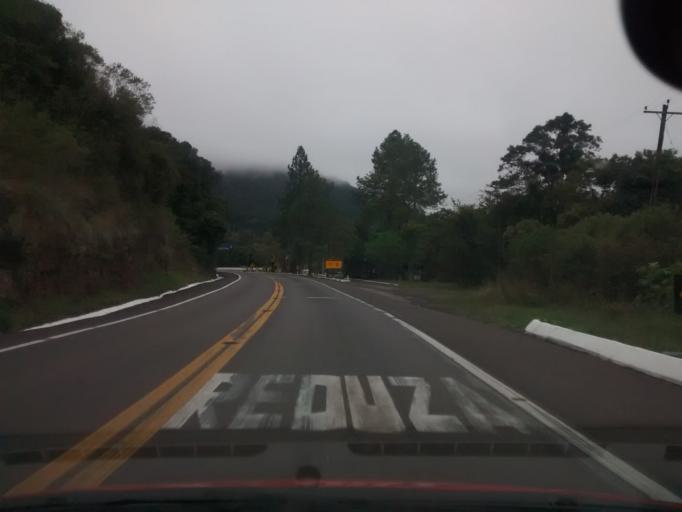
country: BR
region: Rio Grande do Sul
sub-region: Vacaria
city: Estrela
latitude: -28.2133
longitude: -50.7585
